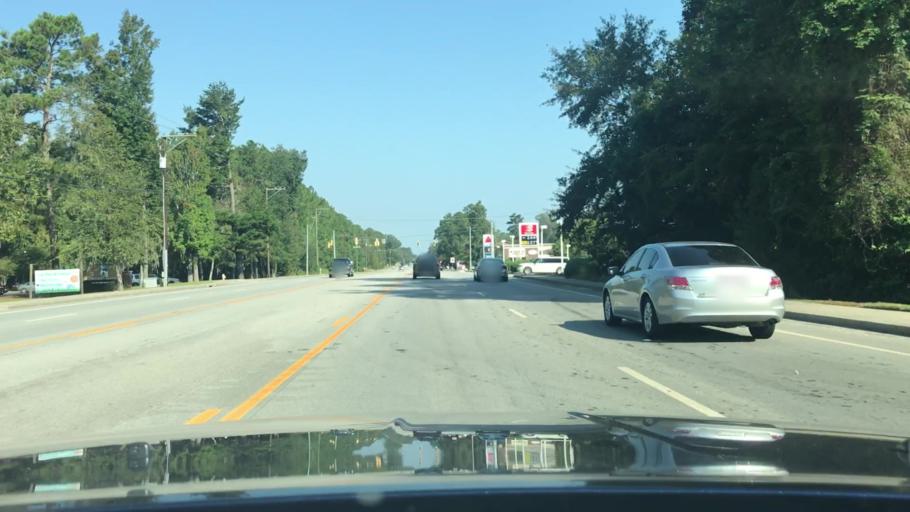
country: US
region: South Carolina
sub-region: Dorchester County
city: Centerville
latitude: 32.9704
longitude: -80.1693
